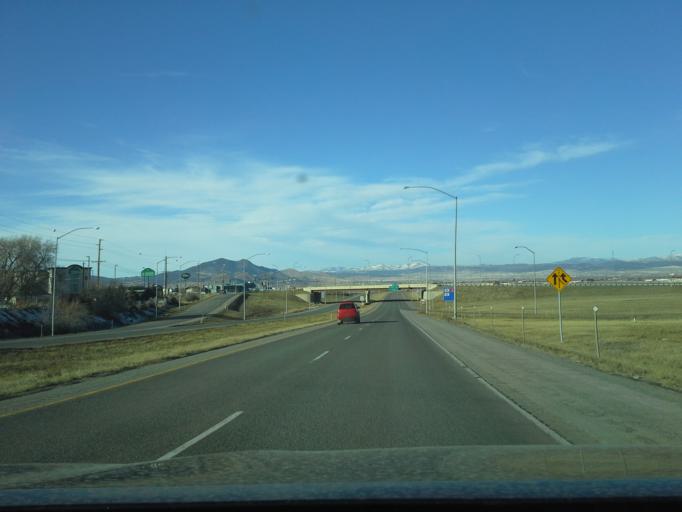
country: US
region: Montana
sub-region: Lewis and Clark County
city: Helena
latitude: 46.6041
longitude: -112.0063
